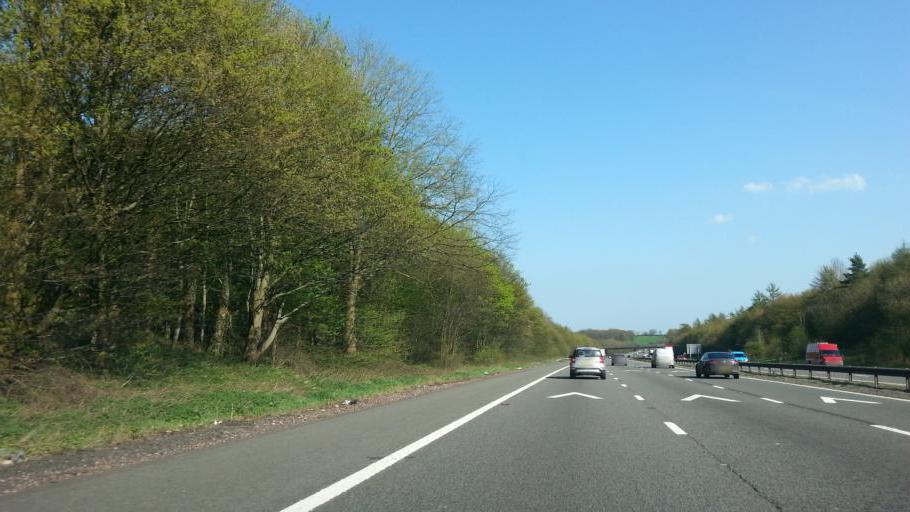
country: GB
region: England
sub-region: Warwickshire
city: Long Lawford
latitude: 52.4331
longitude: -1.3394
